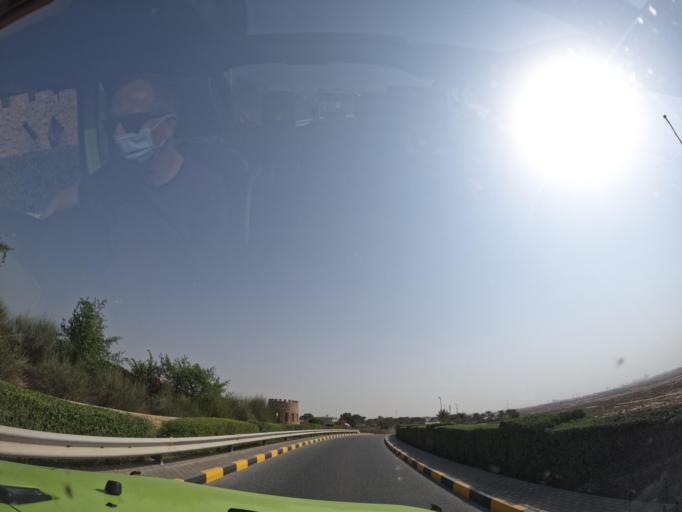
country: AE
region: Umm al Qaywayn
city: Umm al Qaywayn
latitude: 25.4763
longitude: 55.5259
